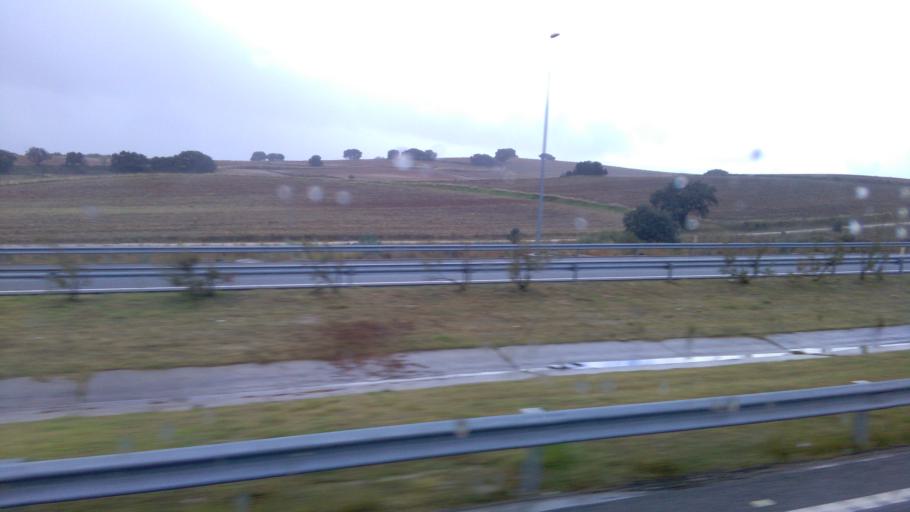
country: ES
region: Madrid
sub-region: Provincia de Madrid
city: El Alamo
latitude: 40.2621
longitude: -3.9685
